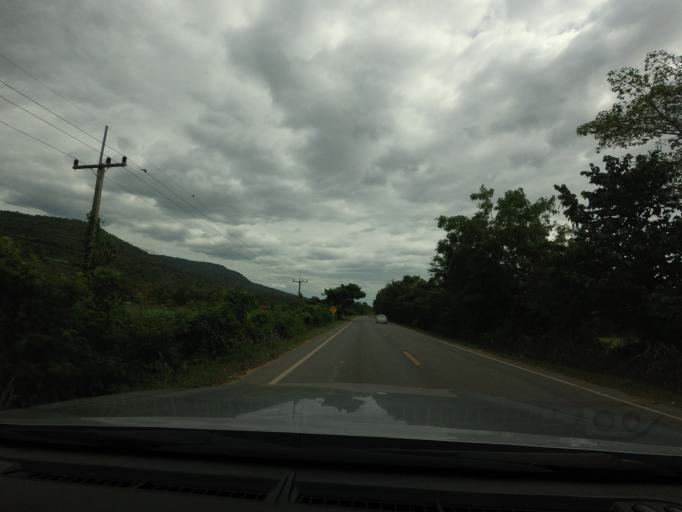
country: TH
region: Phitsanulok
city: Noen Maprang
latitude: 16.7064
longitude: 100.5815
